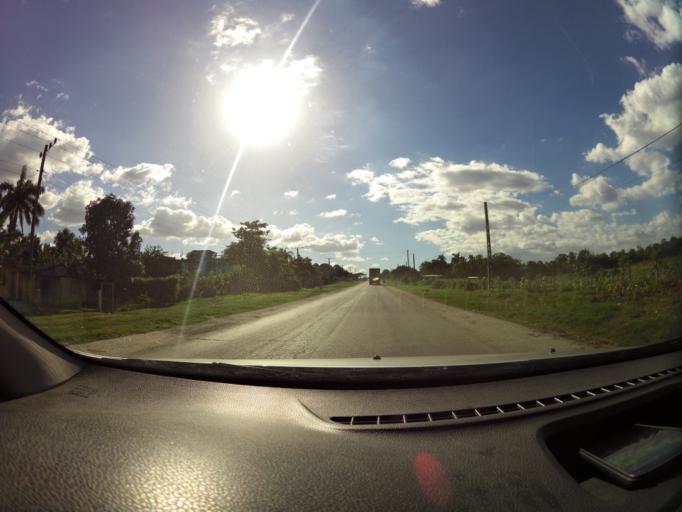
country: CU
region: Santiago de Cuba
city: Palma Soriano
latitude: 20.2320
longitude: -76.0174
